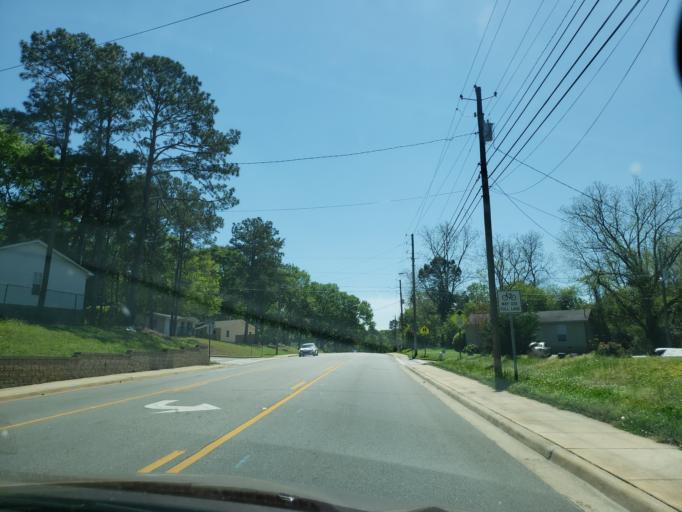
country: US
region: Alabama
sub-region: Lee County
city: Auburn
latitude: 32.6211
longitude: -85.4925
